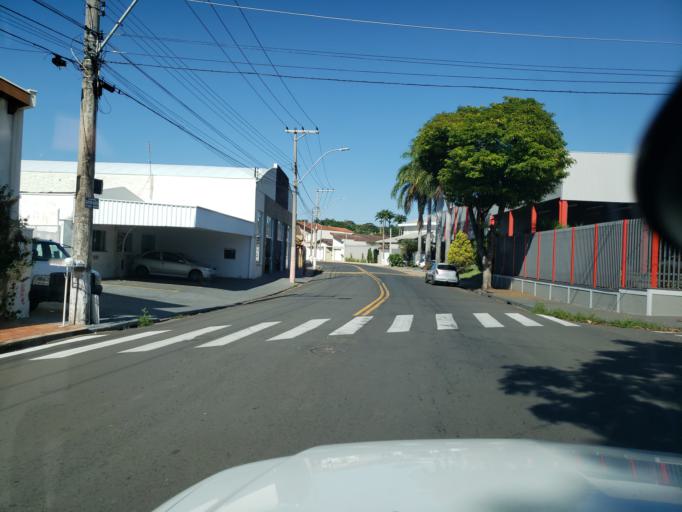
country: BR
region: Sao Paulo
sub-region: Itapira
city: Itapira
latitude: -22.4419
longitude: -46.8320
